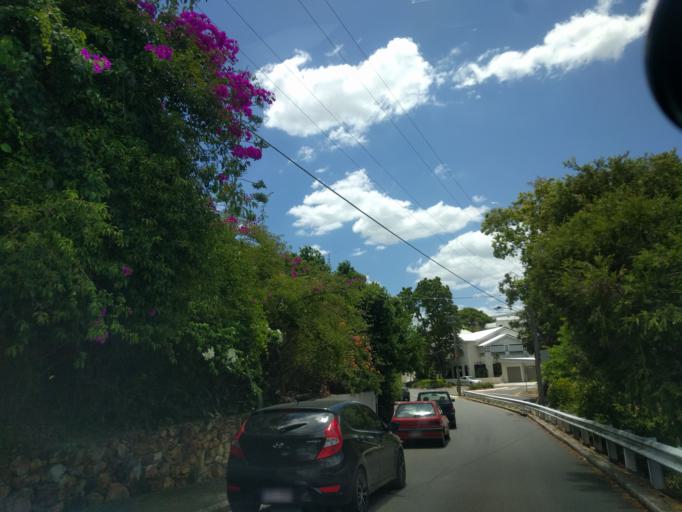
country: AU
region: Queensland
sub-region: Brisbane
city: Fortitude Valley
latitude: -27.4599
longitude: 153.0470
